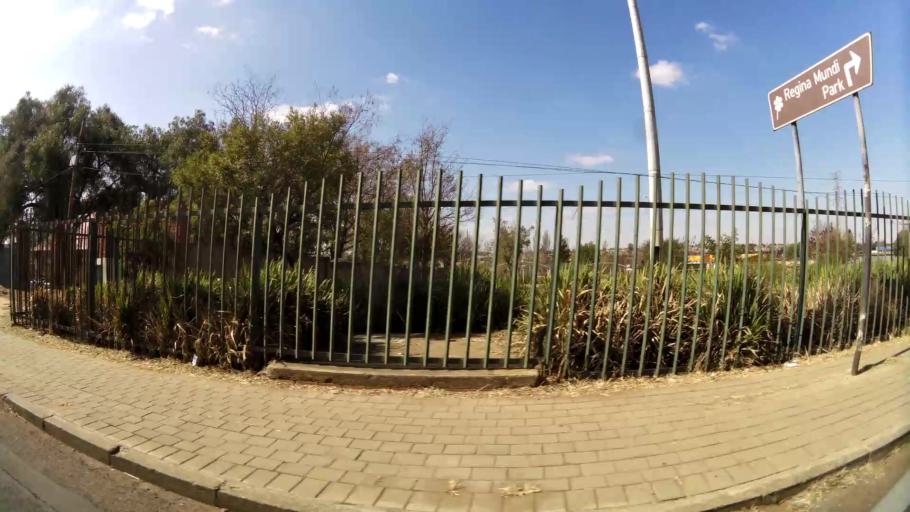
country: ZA
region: Gauteng
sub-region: City of Johannesburg Metropolitan Municipality
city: Soweto
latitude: -26.2614
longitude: 27.8852
